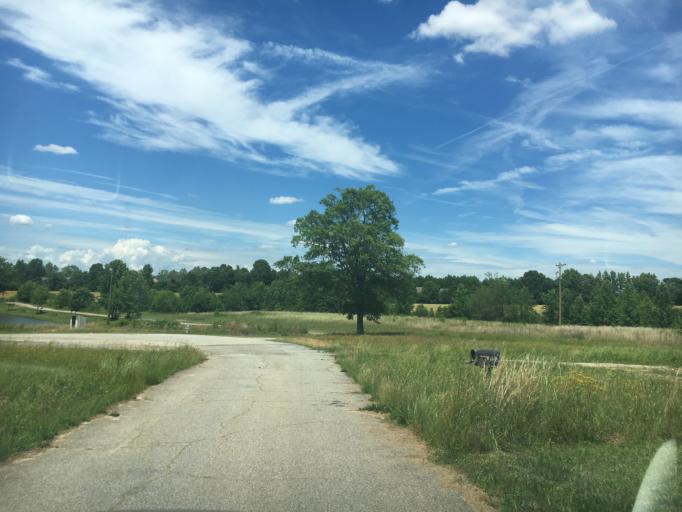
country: US
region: South Carolina
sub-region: Spartanburg County
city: Duncan
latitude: 34.8524
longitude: -82.1501
